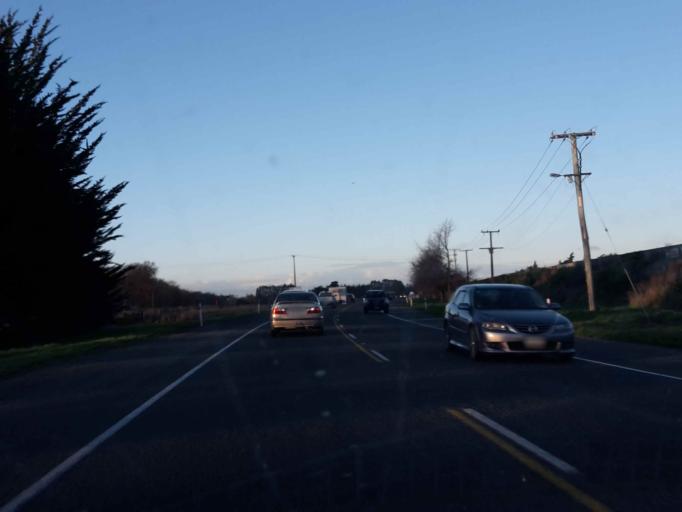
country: NZ
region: Canterbury
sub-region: Selwyn District
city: Rolleston
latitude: -43.5858
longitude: 172.3918
